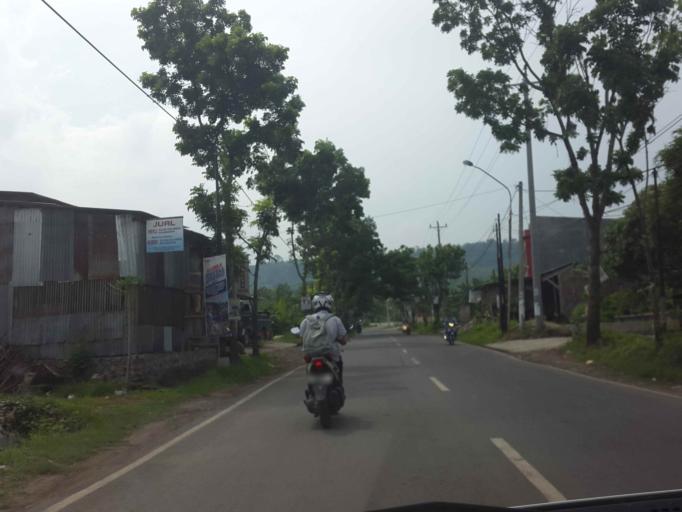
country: ID
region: Central Java
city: Mranggen
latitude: -7.0574
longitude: 110.4625
